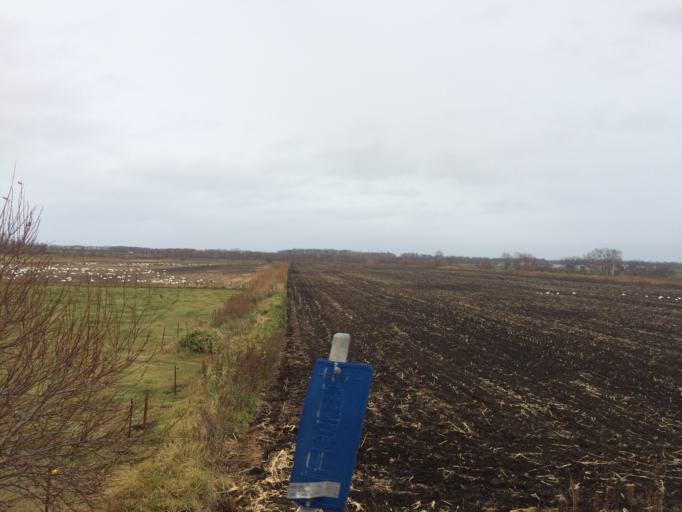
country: JP
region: Hokkaido
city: Abashiri
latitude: 43.8922
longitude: 144.4767
